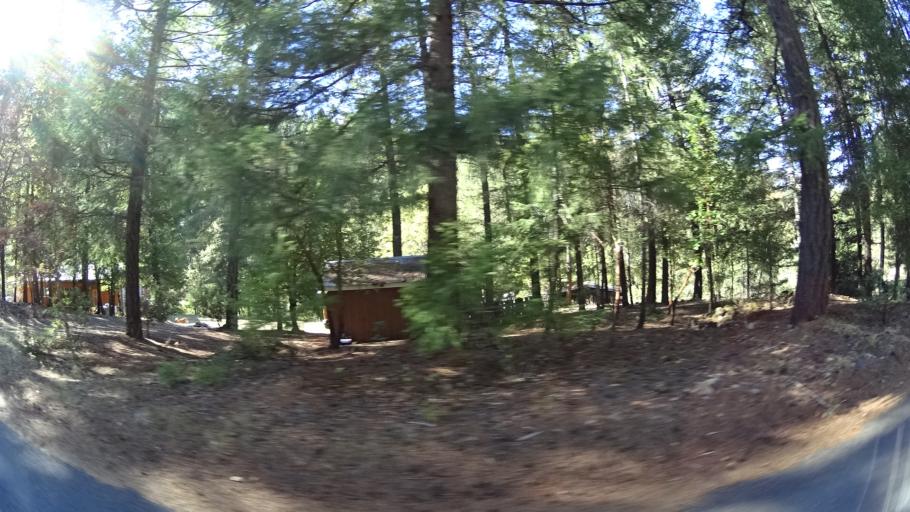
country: US
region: California
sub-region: Trinity County
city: Weaverville
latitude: 41.1417
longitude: -123.1484
